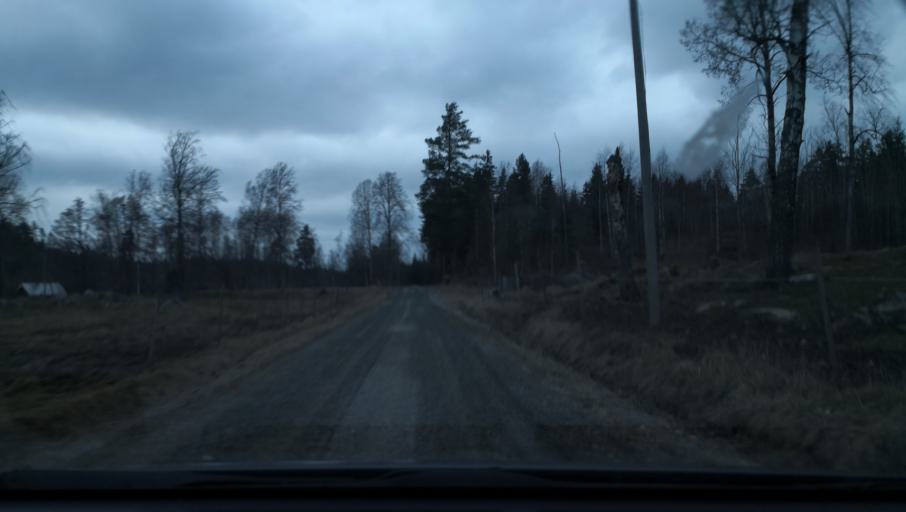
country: SE
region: OErebro
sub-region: Lindesbergs Kommun
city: Fellingsbro
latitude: 59.6077
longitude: 15.6089
